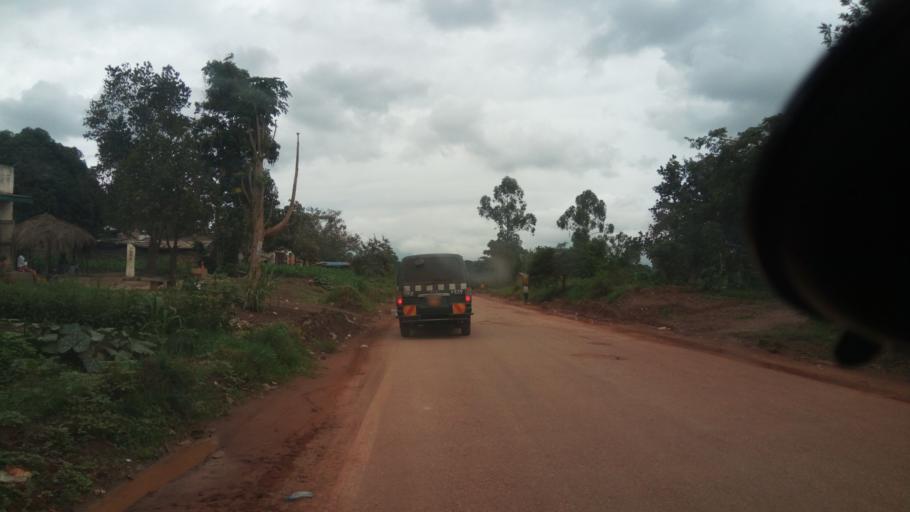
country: UG
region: Central Region
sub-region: Nakaseke District
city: Namasuba
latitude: 0.5467
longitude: 32.2326
